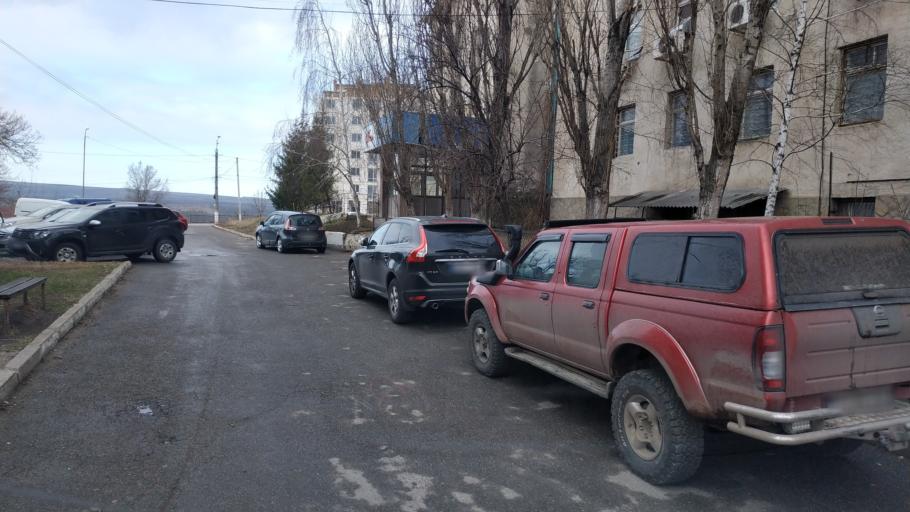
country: MD
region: Laloveni
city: Ialoveni
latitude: 46.9500
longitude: 28.7739
